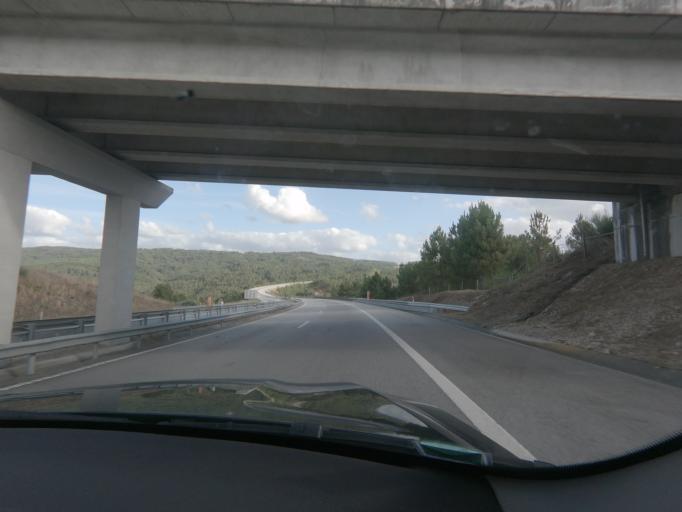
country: PT
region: Viseu
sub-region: Viseu
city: Campo
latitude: 40.8029
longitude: -7.9317
